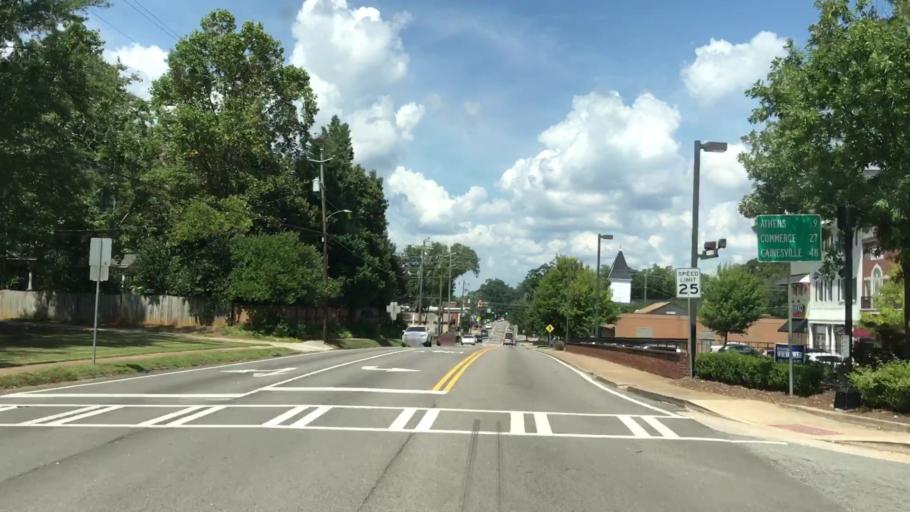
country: US
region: Georgia
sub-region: Oconee County
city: Watkinsville
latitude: 33.8611
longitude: -83.4075
